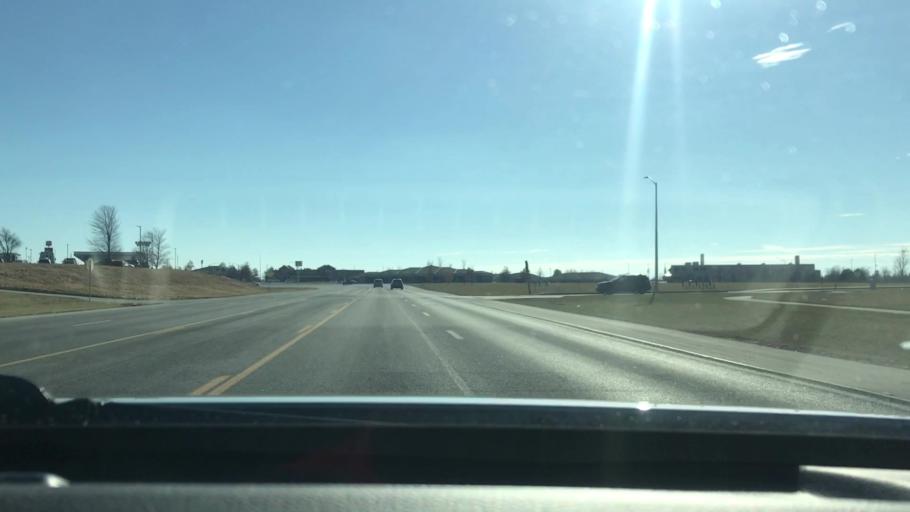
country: US
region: Missouri
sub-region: Platte County
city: Platte City
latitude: 39.3572
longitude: -94.7692
